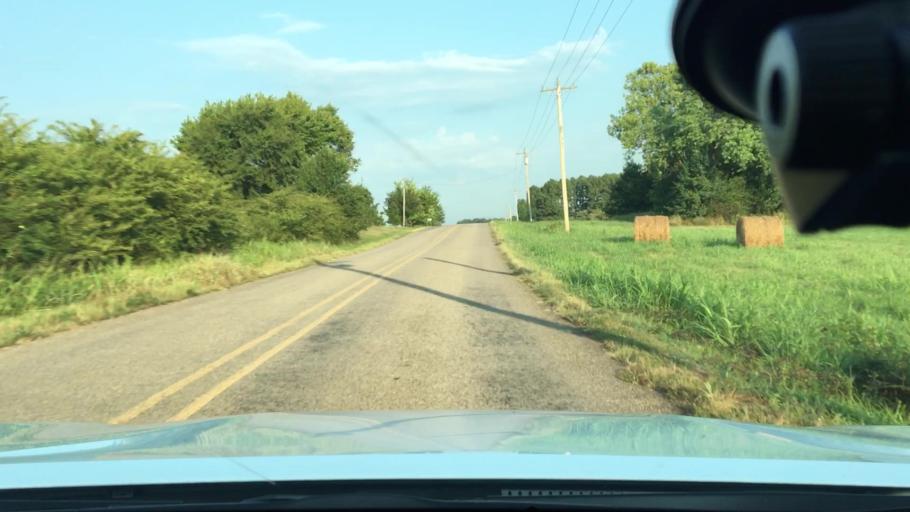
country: US
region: Arkansas
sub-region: Johnson County
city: Coal Hill
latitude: 35.3711
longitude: -93.5795
